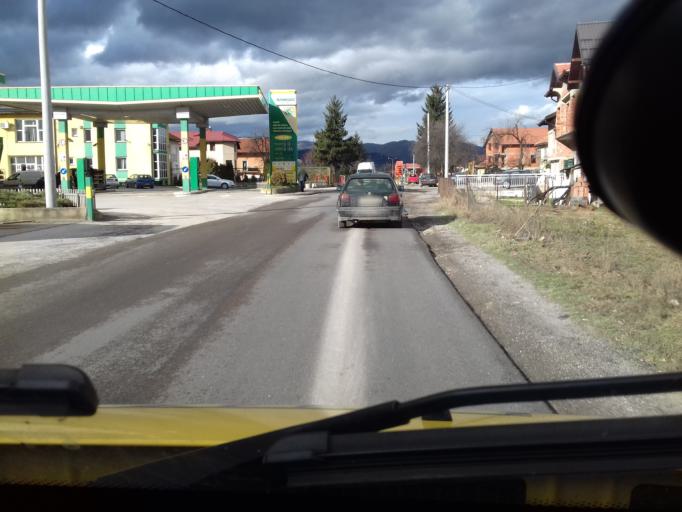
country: BA
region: Federation of Bosnia and Herzegovina
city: Gornje Mostre
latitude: 44.0068
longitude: 18.1532
